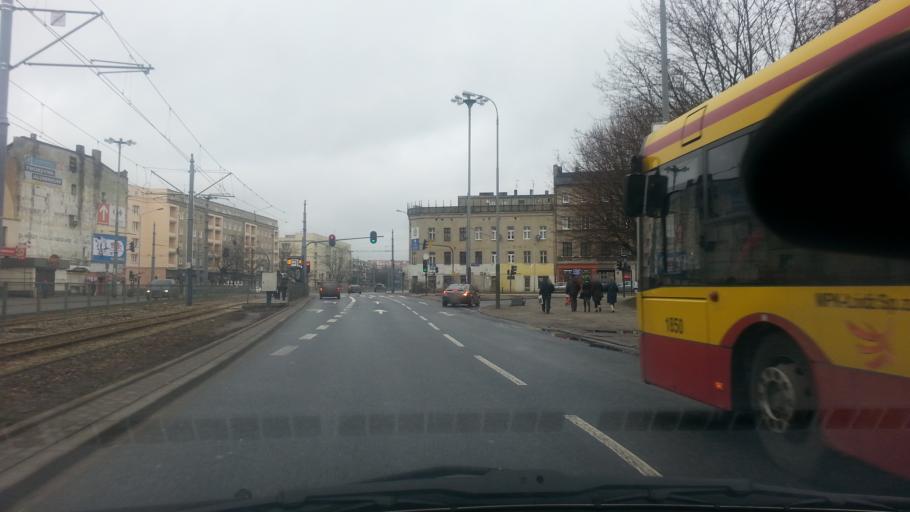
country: PL
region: Lodz Voivodeship
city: Lodz
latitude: 51.7862
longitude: 19.4495
